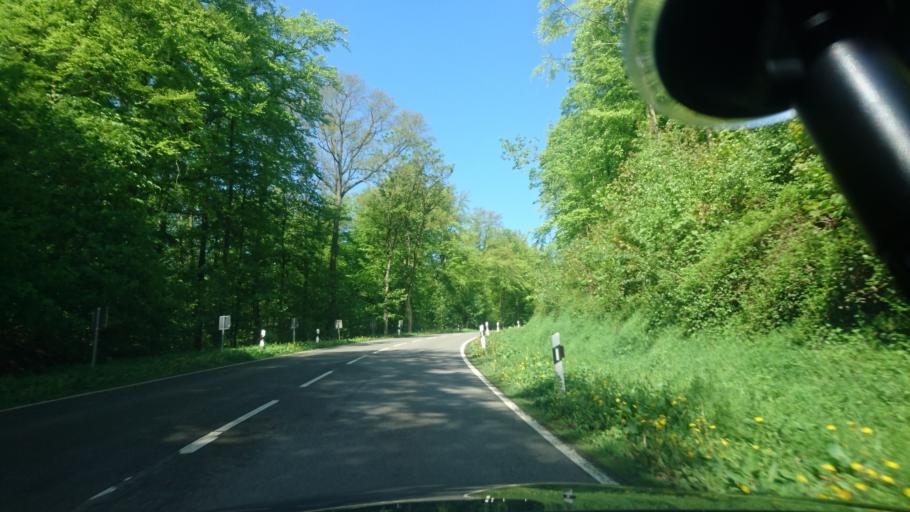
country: DE
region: Hesse
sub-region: Regierungsbezirk Kassel
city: Bad Arolsen
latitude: 51.3827
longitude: 8.9914
